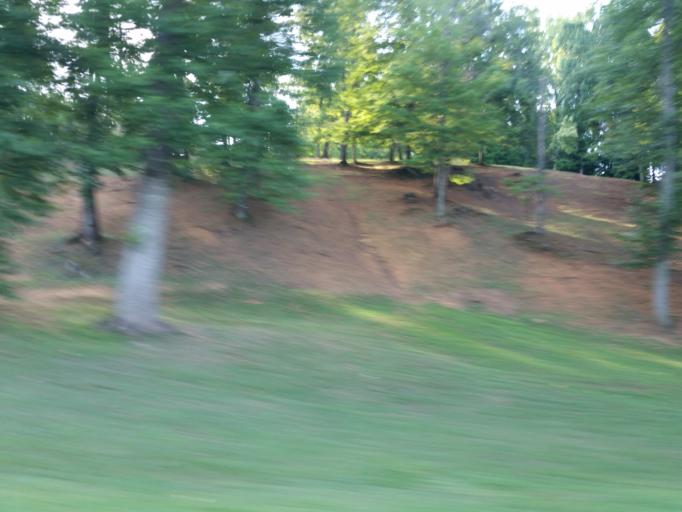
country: US
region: Tennessee
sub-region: Blount County
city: Wildwood
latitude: 35.8481
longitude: -83.8891
